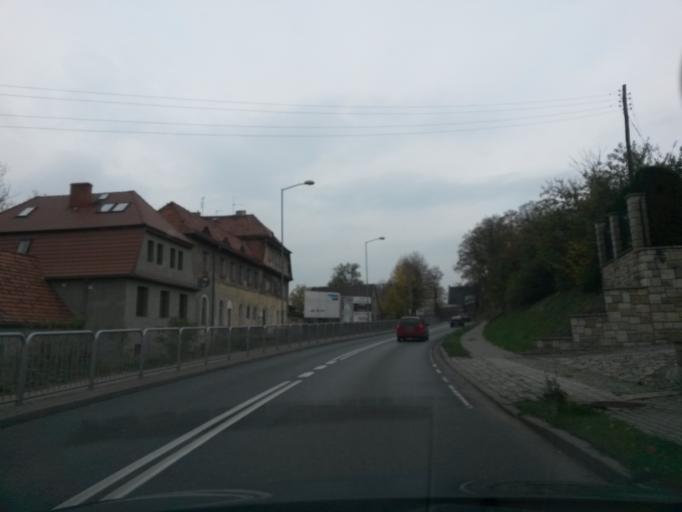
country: PL
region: Lower Silesian Voivodeship
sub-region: Powiat klodzki
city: Klodzko
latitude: 50.4308
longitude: 16.6569
